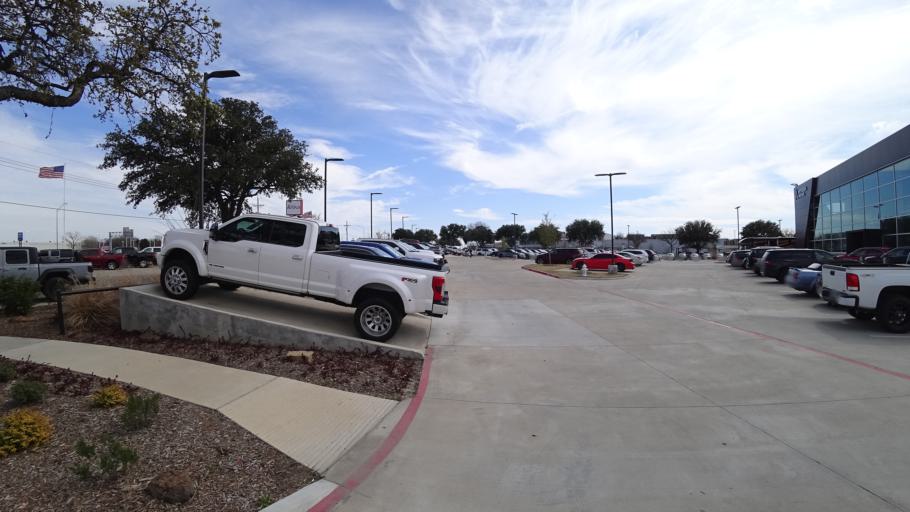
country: US
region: Texas
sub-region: Denton County
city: Lewisville
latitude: 33.0246
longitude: -96.9891
